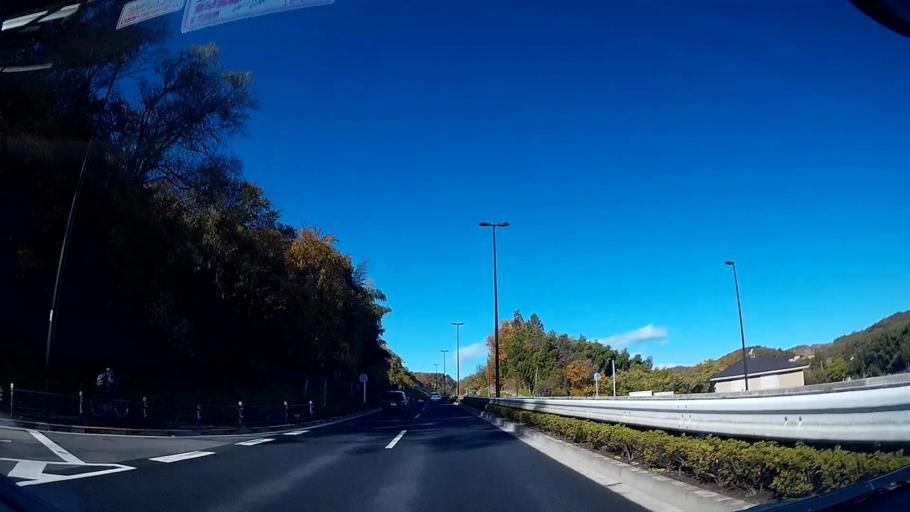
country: JP
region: Tokyo
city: Fussa
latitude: 35.6982
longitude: 139.3168
